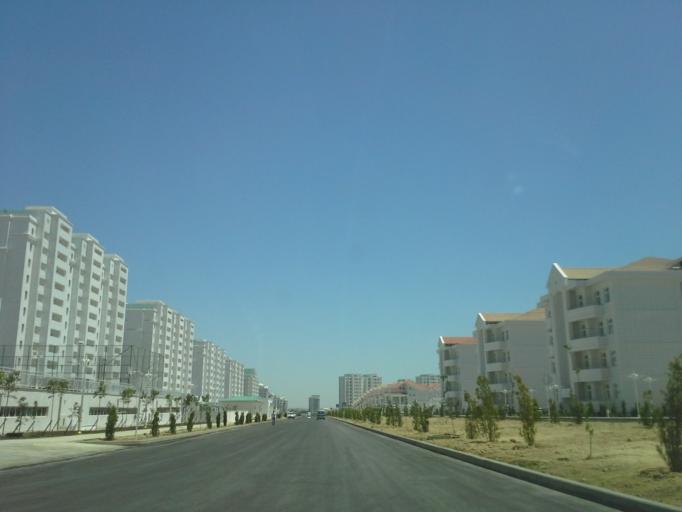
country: TM
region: Ahal
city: Ashgabat
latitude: 37.9388
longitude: 58.3535
